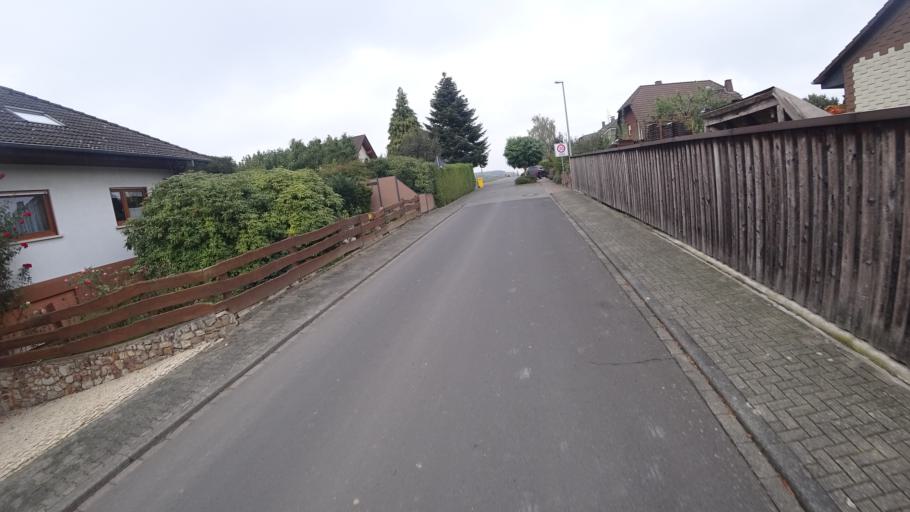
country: DE
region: Rheinland-Pfalz
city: Eppenrod
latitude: 50.4070
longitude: 7.9305
